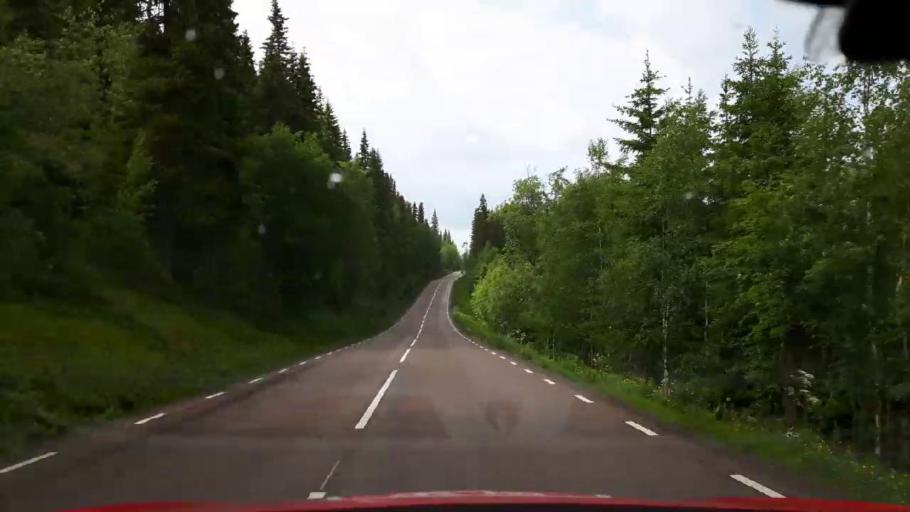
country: SE
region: Jaemtland
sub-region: Krokoms Kommun
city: Valla
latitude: 63.9506
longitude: 14.2151
